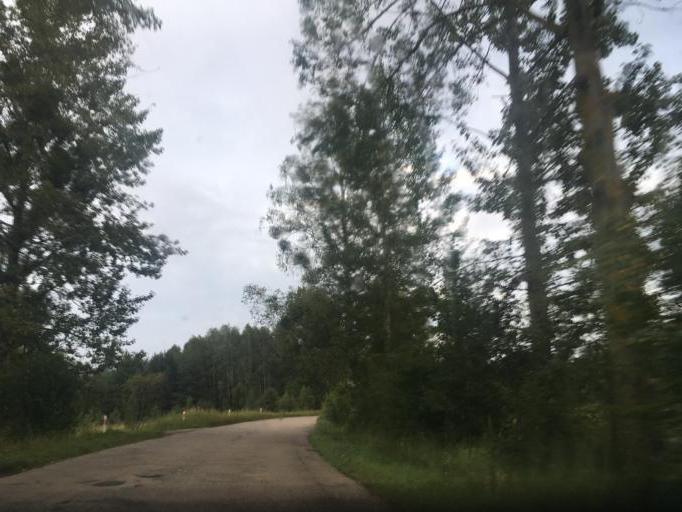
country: PL
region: Podlasie
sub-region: Powiat hajnowski
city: Hajnowka
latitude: 52.8251
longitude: 23.7182
